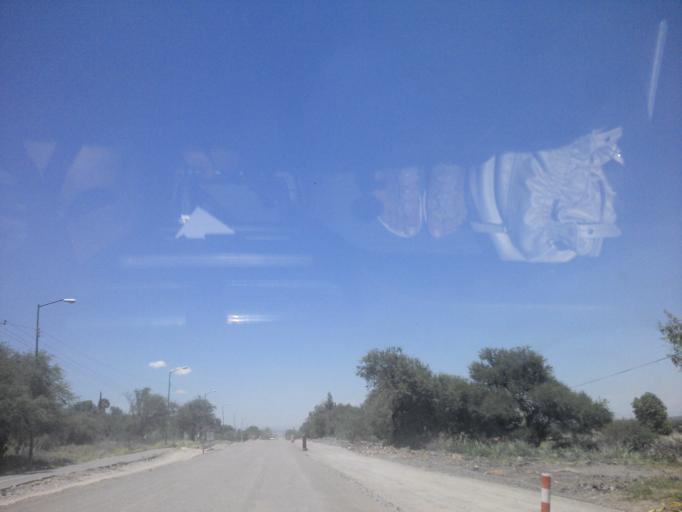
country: MX
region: Guanajuato
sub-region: San Francisco del Rincon
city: San Ignacio de Hidalgo
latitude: 20.9436
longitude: -101.9077
